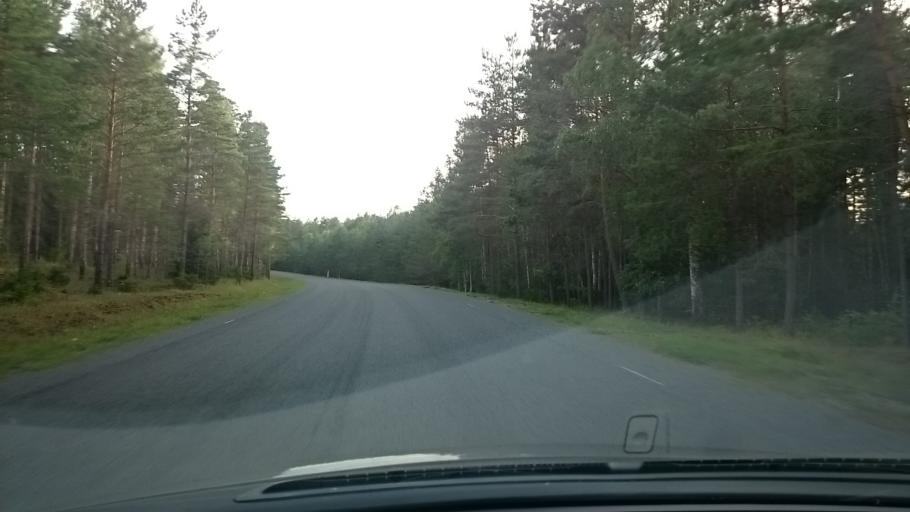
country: EE
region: Saare
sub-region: Kuressaare linn
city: Kuressaare
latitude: 58.4371
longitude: 22.2191
